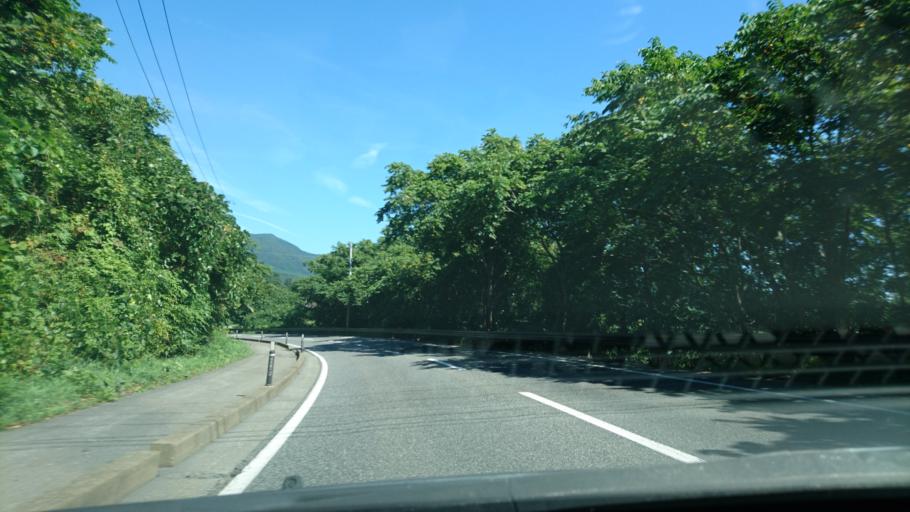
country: JP
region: Iwate
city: Tono
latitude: 39.3349
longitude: 141.5193
